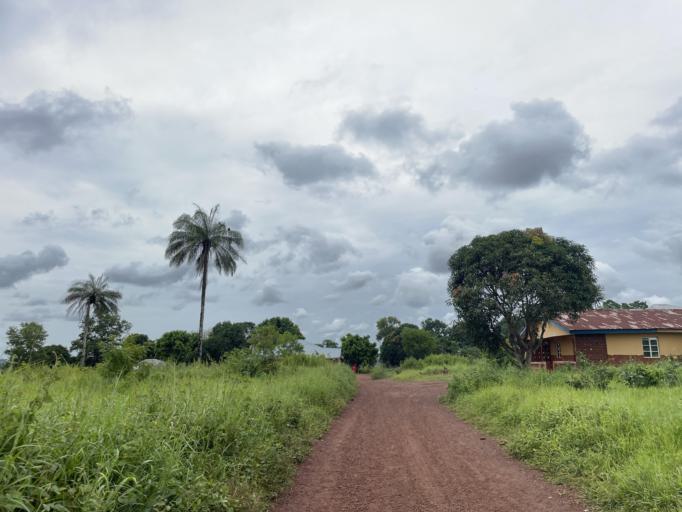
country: SL
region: Northern Province
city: Kambia
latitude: 9.1302
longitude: -12.9098
